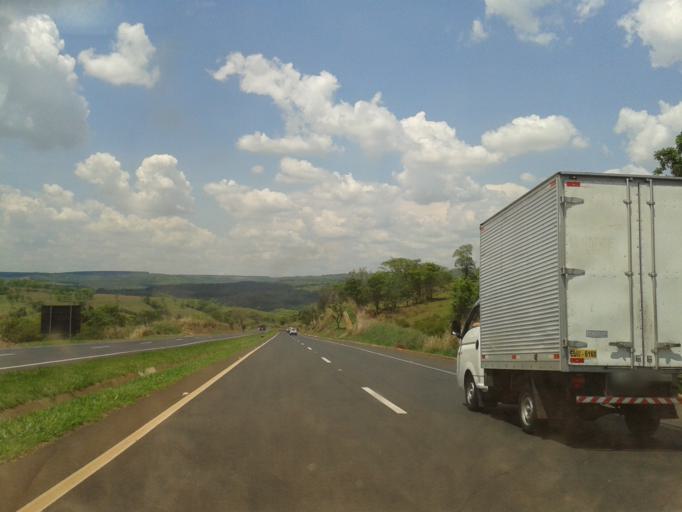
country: BR
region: Minas Gerais
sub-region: Araguari
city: Araguari
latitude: -18.7575
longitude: -48.2407
